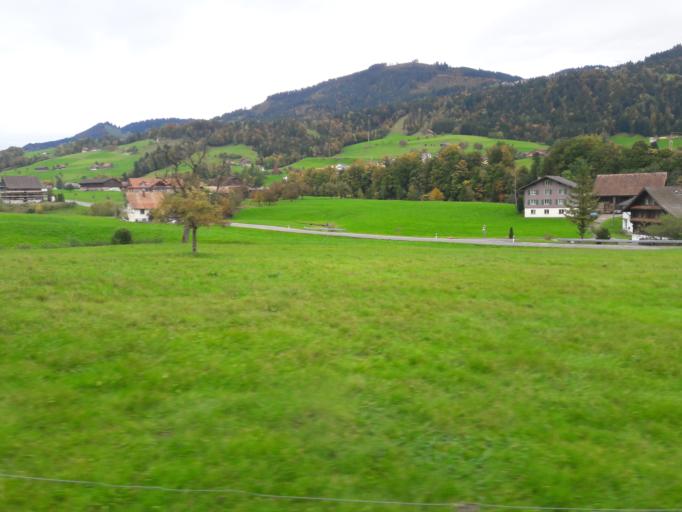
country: CH
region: Schwyz
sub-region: Bezirk Schwyz
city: Sattel
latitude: 47.0772
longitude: 8.6249
